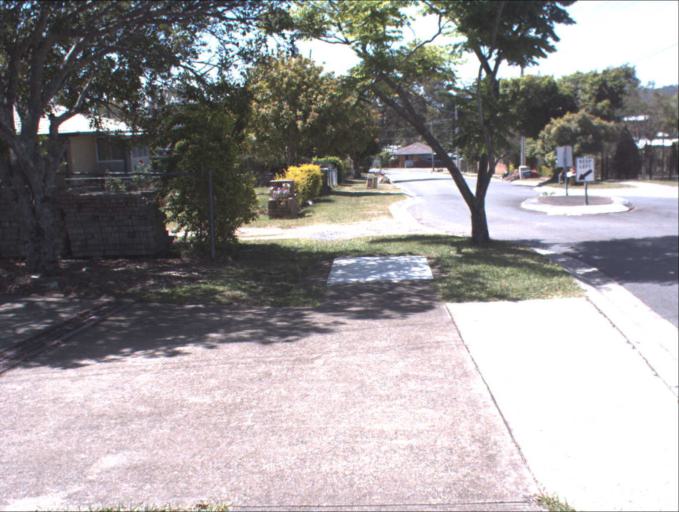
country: AU
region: Queensland
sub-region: Logan
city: Logan City
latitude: -27.6473
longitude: 153.1268
